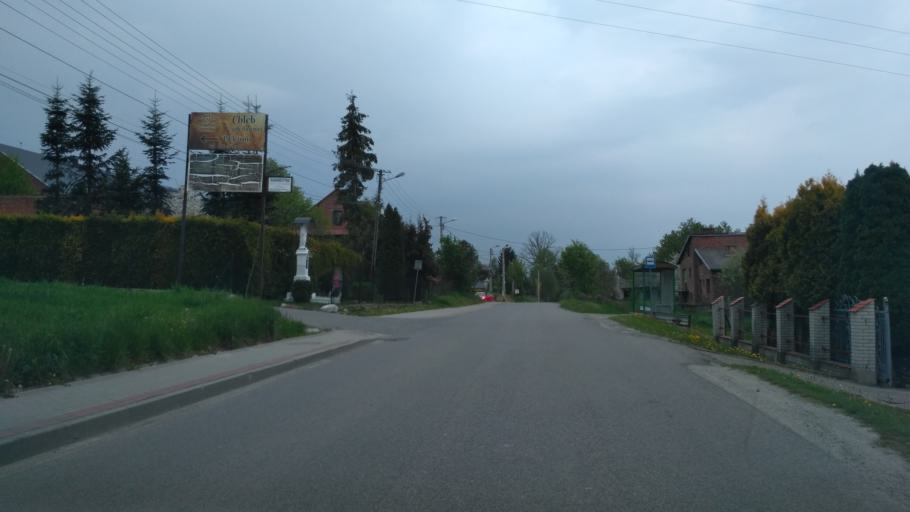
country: PL
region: Lesser Poland Voivodeship
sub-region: Powiat tarnowski
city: Skrzyszow
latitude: 49.9663
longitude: 21.0492
